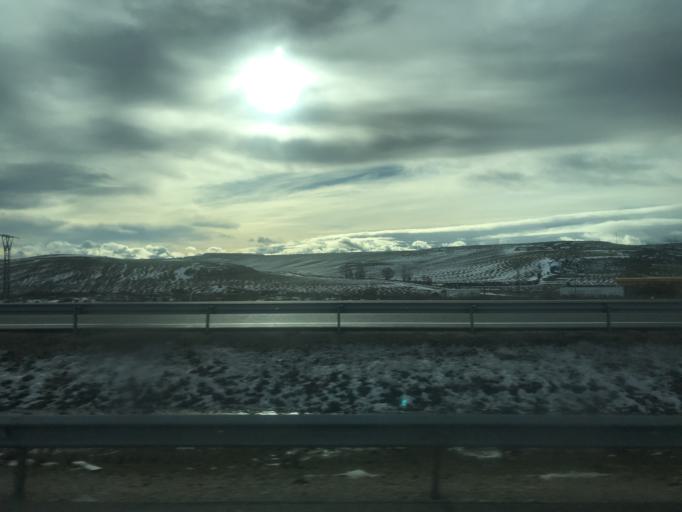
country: ES
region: Castille and Leon
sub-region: Provincia de Burgos
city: Quintanapalla
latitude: 42.4188
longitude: -3.5210
